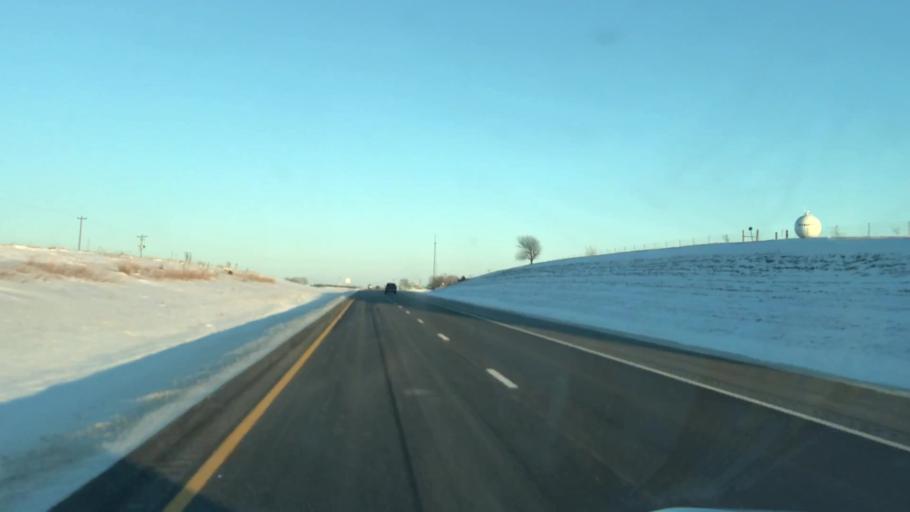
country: US
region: Missouri
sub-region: Clinton County
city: Gower
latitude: 39.7620
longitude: -94.5108
